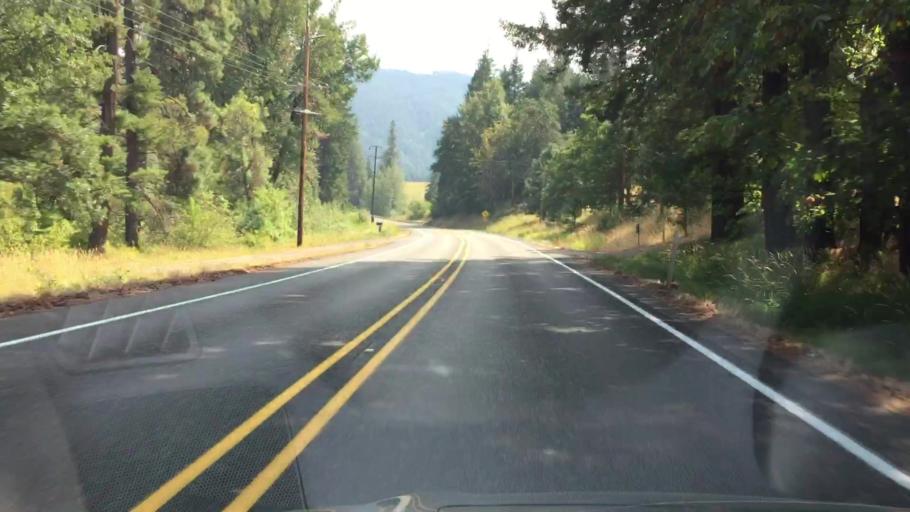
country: US
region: Washington
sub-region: Klickitat County
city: White Salmon
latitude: 45.8077
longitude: -121.4909
